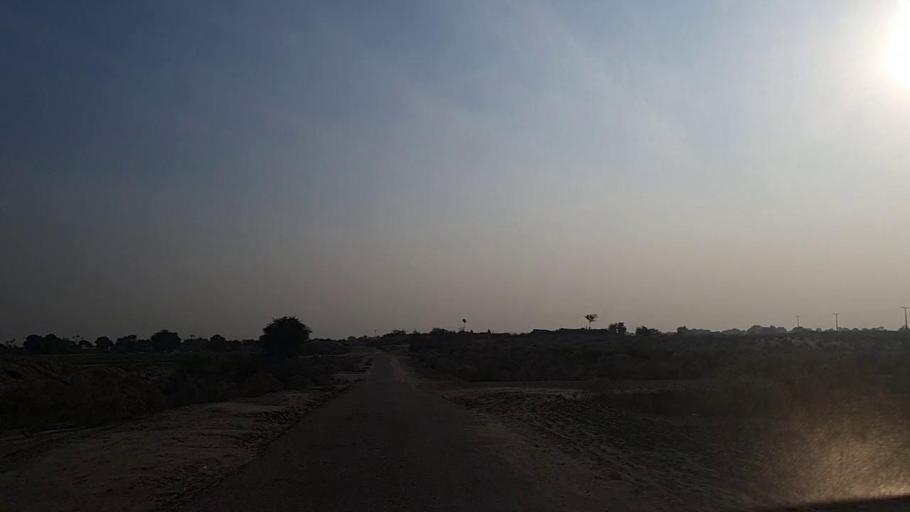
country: PK
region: Sindh
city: Jam Sahib
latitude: 26.4388
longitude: 68.5937
